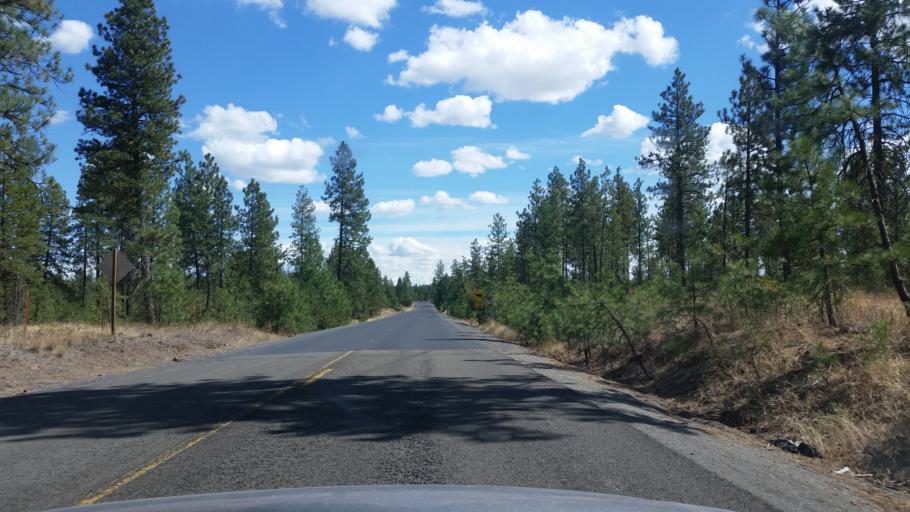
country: US
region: Washington
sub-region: Spokane County
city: Medical Lake
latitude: 47.5038
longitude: -117.6874
